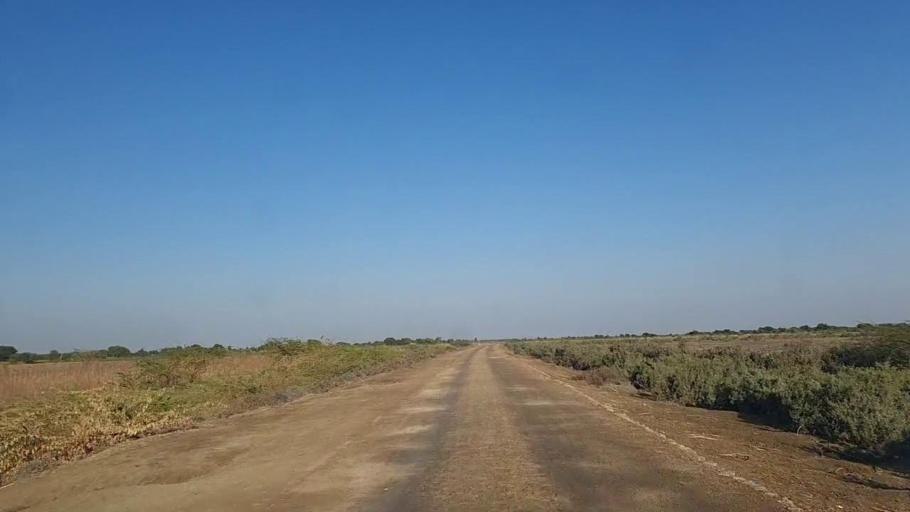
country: PK
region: Sindh
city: Naukot
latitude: 24.9675
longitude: 69.3845
